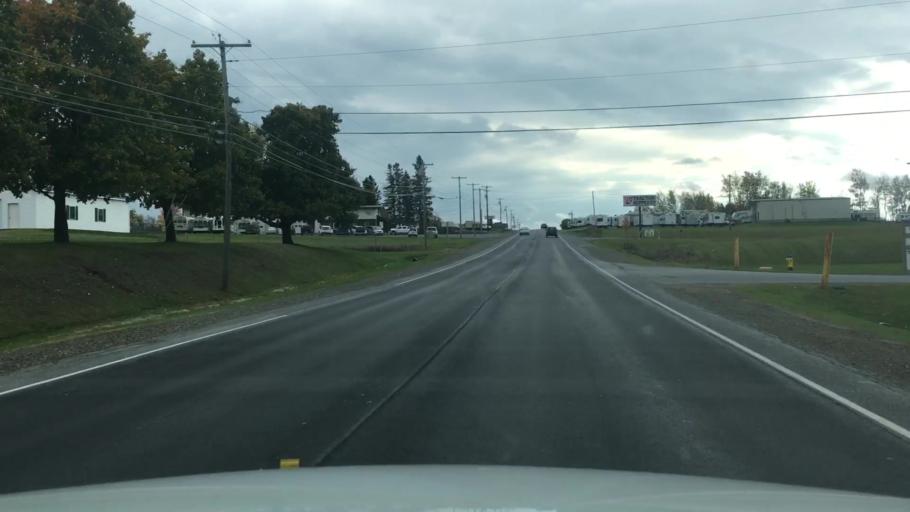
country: US
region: Maine
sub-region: Aroostook County
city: Presque Isle
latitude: 46.6622
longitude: -68.0089
